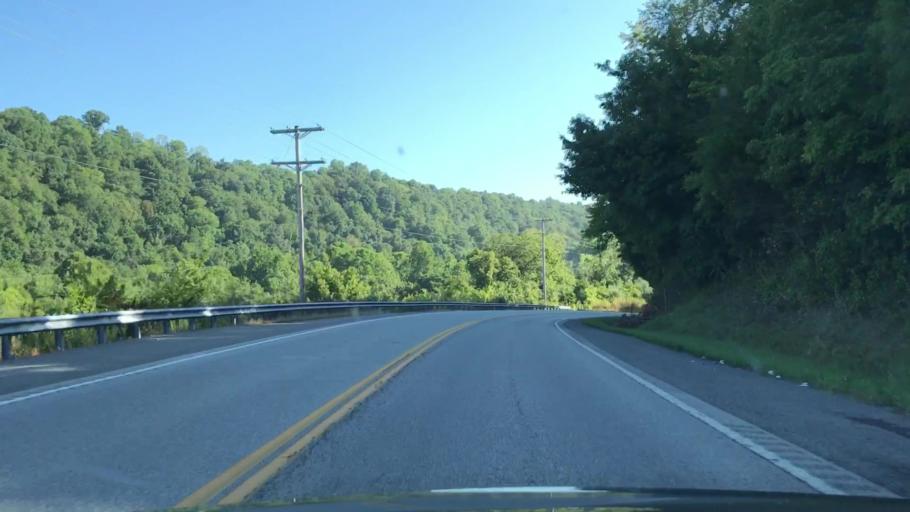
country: US
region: Tennessee
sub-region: Clay County
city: Celina
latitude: 36.4968
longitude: -85.5586
